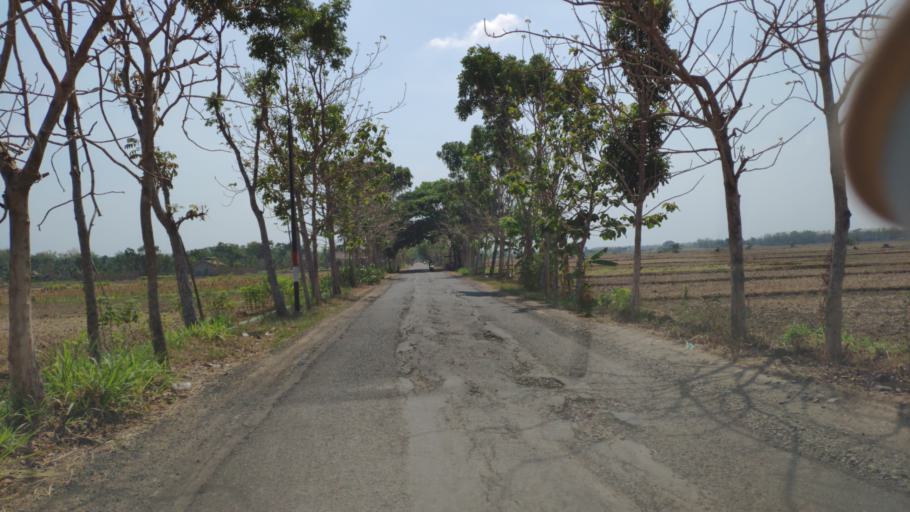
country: ID
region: Central Java
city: Kedungjenar
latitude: -6.9802
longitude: 111.4259
